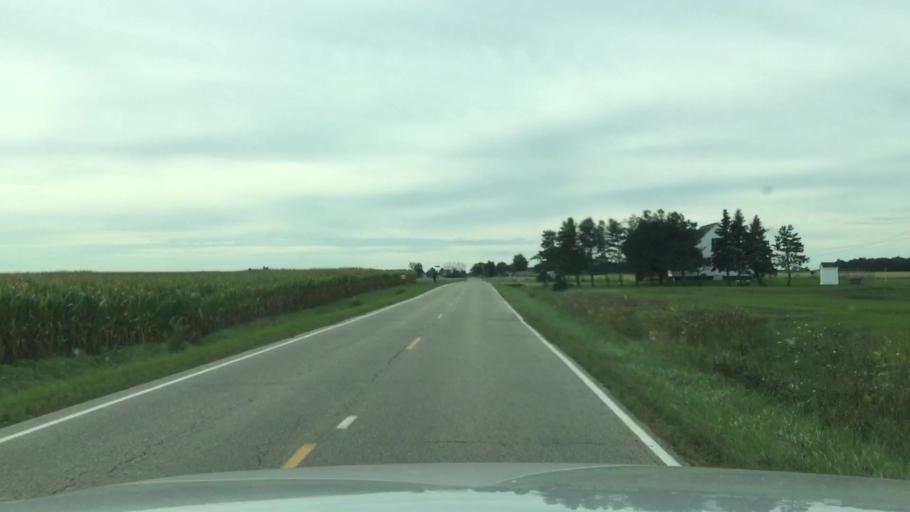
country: US
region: Michigan
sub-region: Genesee County
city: Montrose
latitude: 43.0964
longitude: -83.9878
